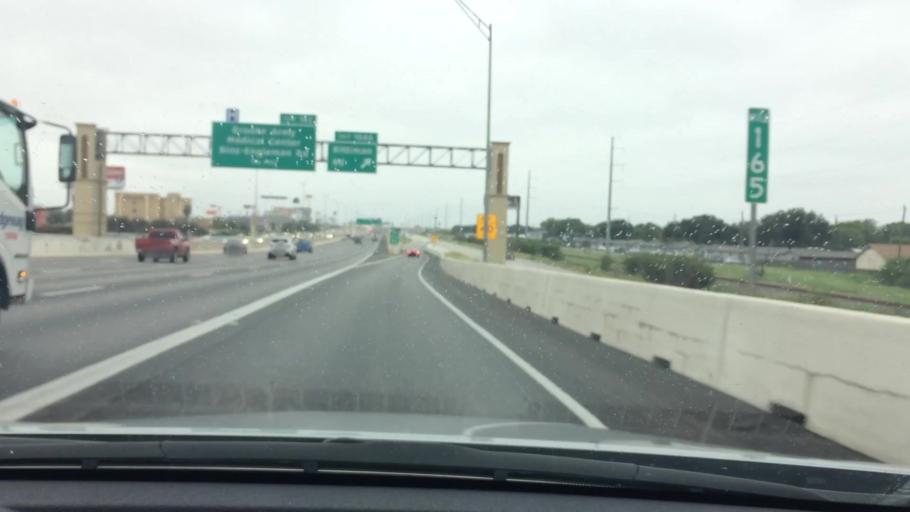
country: US
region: Texas
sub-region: Bexar County
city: Windcrest
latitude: 29.4954
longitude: -98.4010
